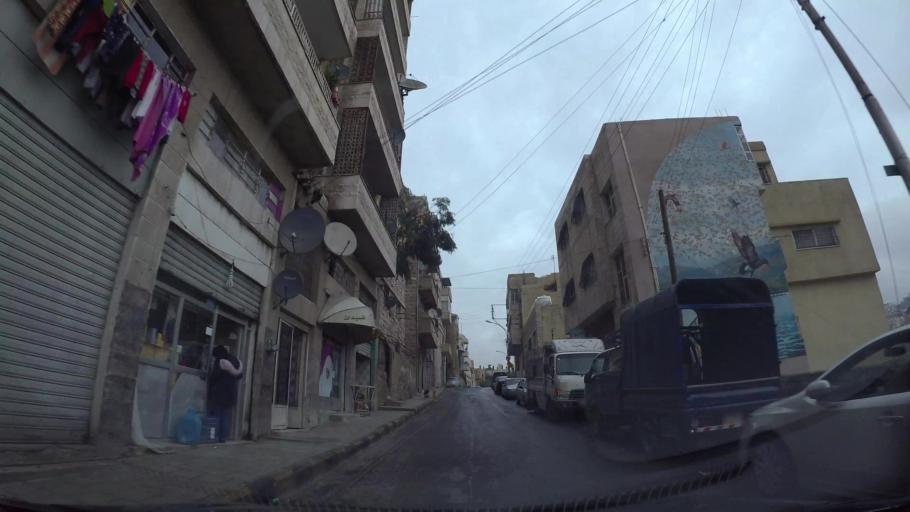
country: JO
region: Amman
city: Amman
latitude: 31.9539
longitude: 35.9406
